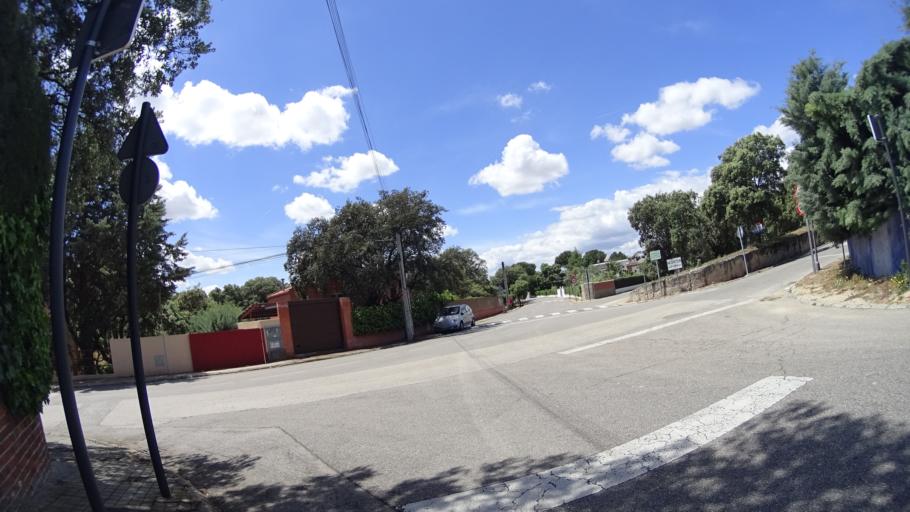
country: ES
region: Madrid
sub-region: Provincia de Madrid
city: Brunete
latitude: 40.4226
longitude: -3.9713
